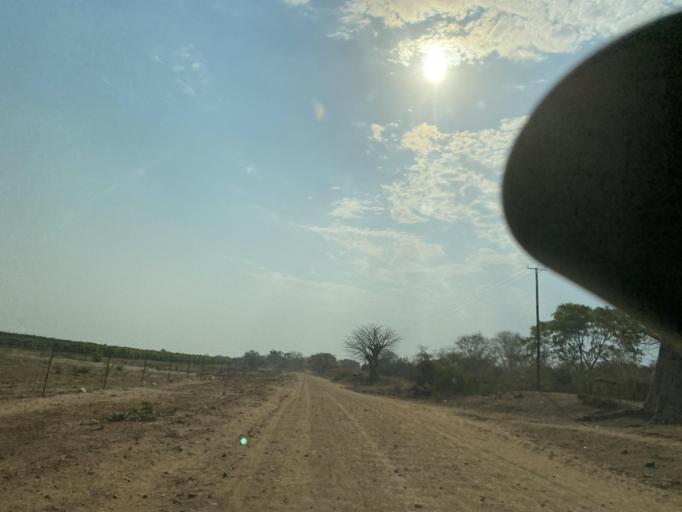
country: ZW
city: Chirundu
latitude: -15.9311
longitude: 28.9556
